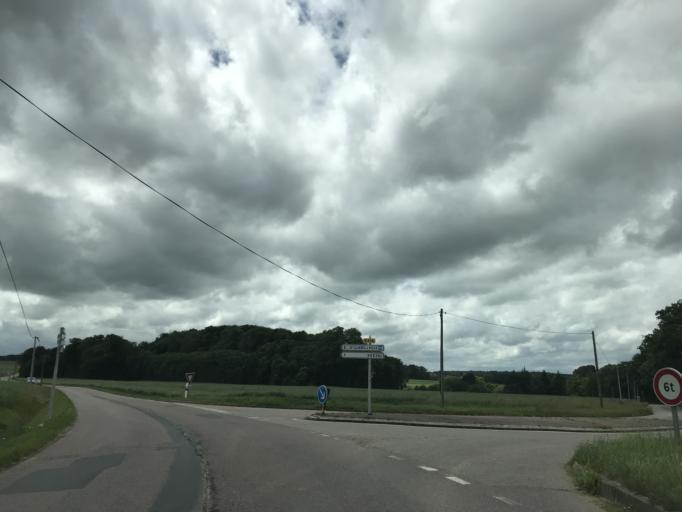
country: FR
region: Ile-de-France
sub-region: Departement des Yvelines
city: Breval
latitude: 48.9736
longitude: 1.5729
